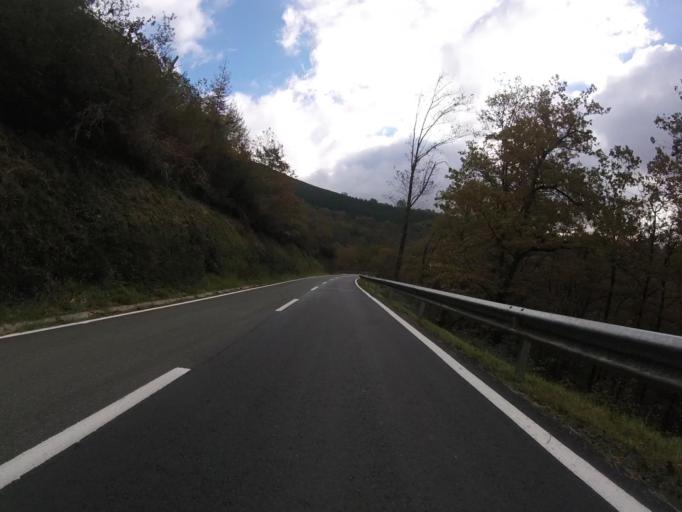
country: ES
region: Navarre
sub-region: Provincia de Navarra
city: Goizueta
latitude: 43.2072
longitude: -1.8581
